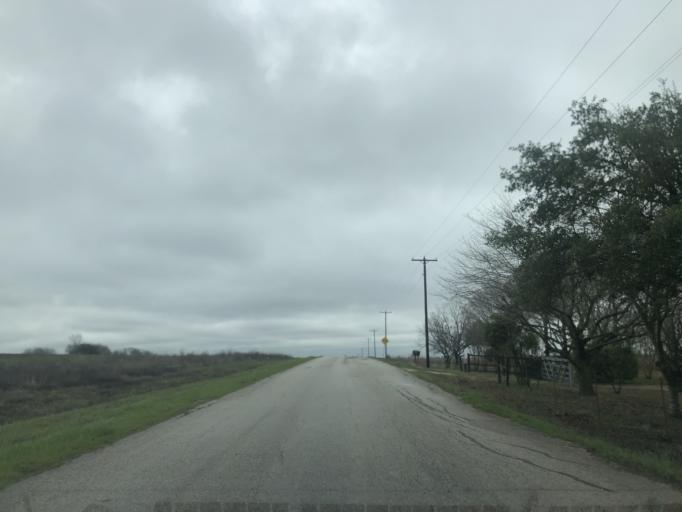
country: US
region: Texas
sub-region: Williamson County
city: Hutto
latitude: 30.5923
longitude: -97.5010
